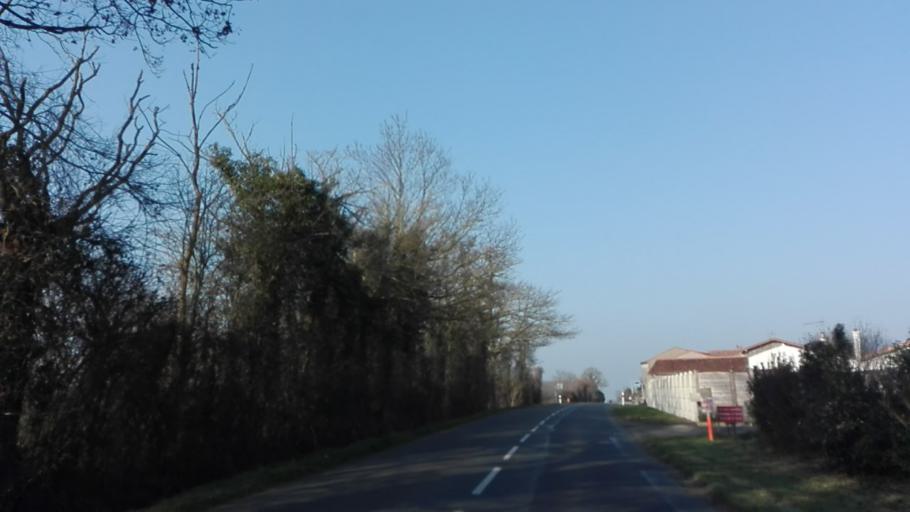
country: FR
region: Pays de la Loire
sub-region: Departement de la Vendee
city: Saint-Georges-de-Montaigu
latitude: 46.9226
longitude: -1.3158
